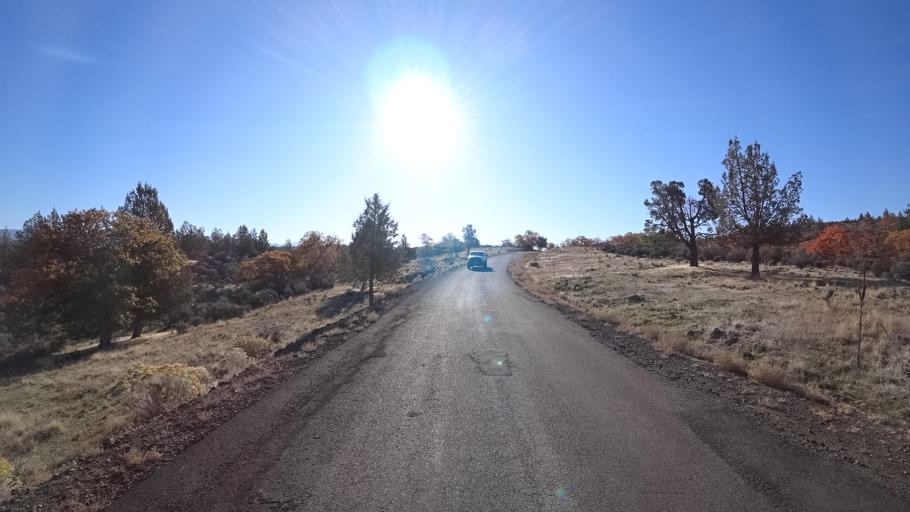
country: US
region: California
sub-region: Siskiyou County
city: Montague
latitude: 41.9094
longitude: -122.4366
